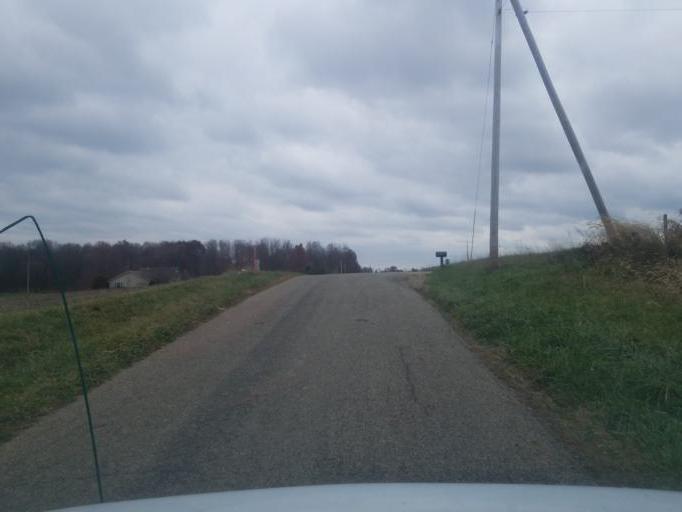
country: US
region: Ohio
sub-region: Knox County
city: Fredericktown
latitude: 40.4734
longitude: -82.5110
